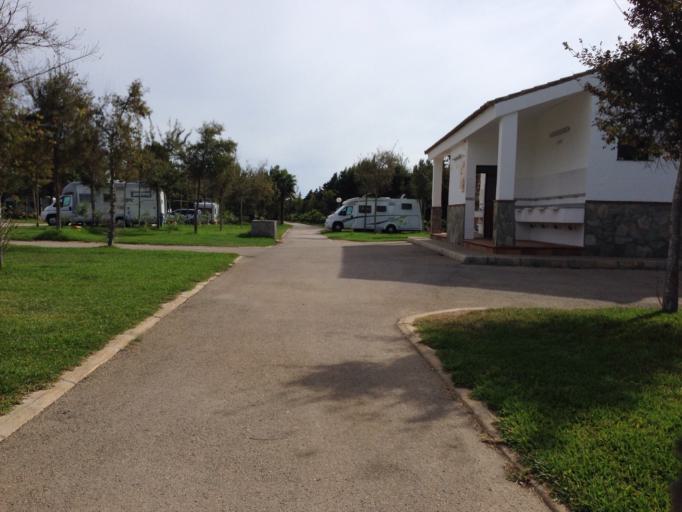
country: ES
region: Andalusia
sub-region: Provincia de Cadiz
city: Conil de la Frontera
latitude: 36.3134
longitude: -6.1136
